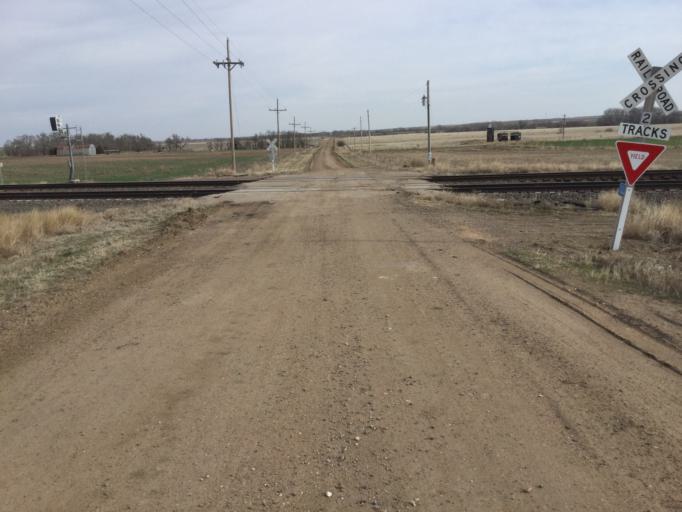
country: US
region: Kansas
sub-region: Ellis County
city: Ellis
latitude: 38.9561
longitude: -99.6692
